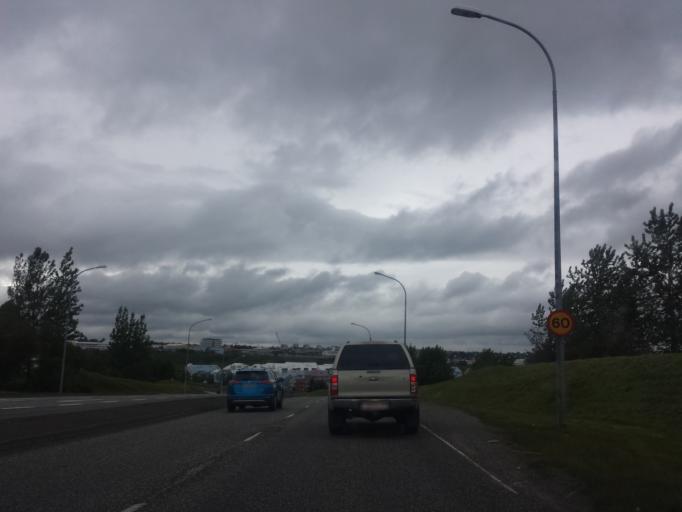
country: IS
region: Capital Region
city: Reykjavik
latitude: 64.1369
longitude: -21.8097
